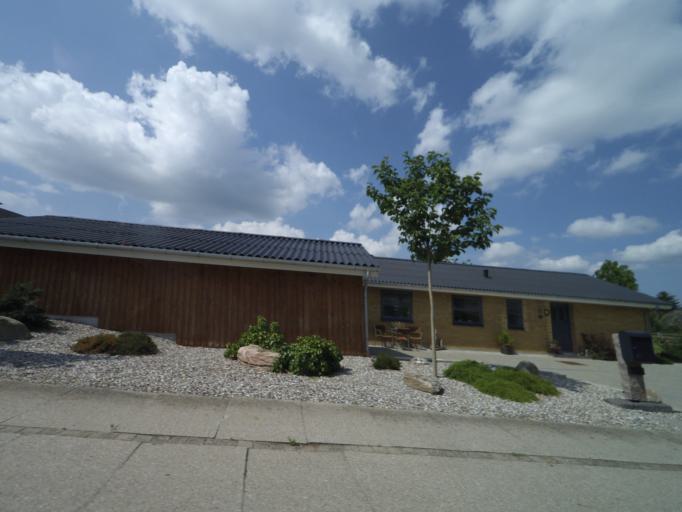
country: DK
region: South Denmark
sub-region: Assens Kommune
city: Arup
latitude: 55.3748
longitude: 10.0405
